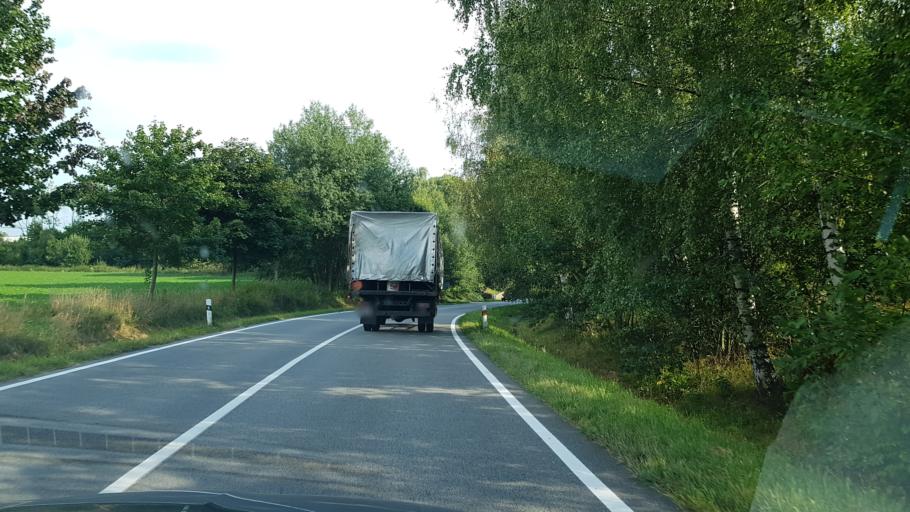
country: PL
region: Lower Silesian Voivodeship
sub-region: Powiat klodzki
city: Miedzylesie
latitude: 50.0979
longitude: 16.6545
